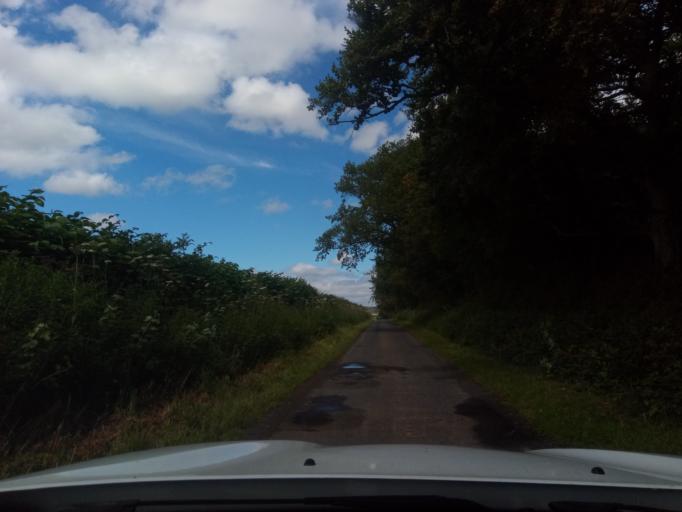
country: GB
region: Scotland
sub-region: The Scottish Borders
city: Jedburgh
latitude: 55.5663
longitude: -2.5461
